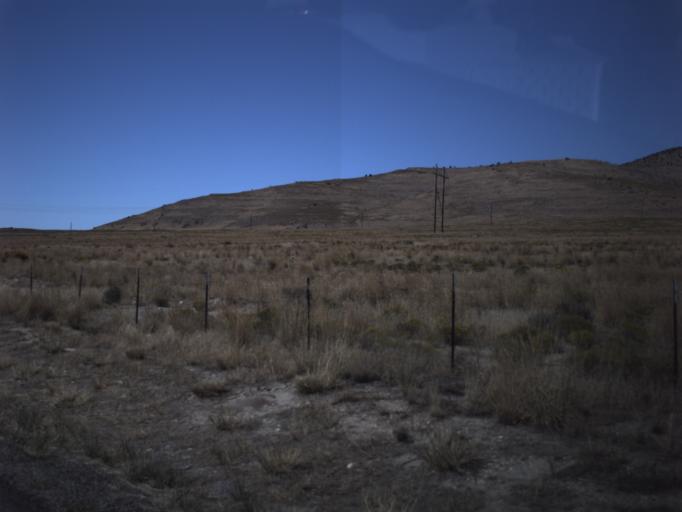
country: US
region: Utah
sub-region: Utah County
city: Eagle Mountain
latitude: 40.1838
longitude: -111.9112
